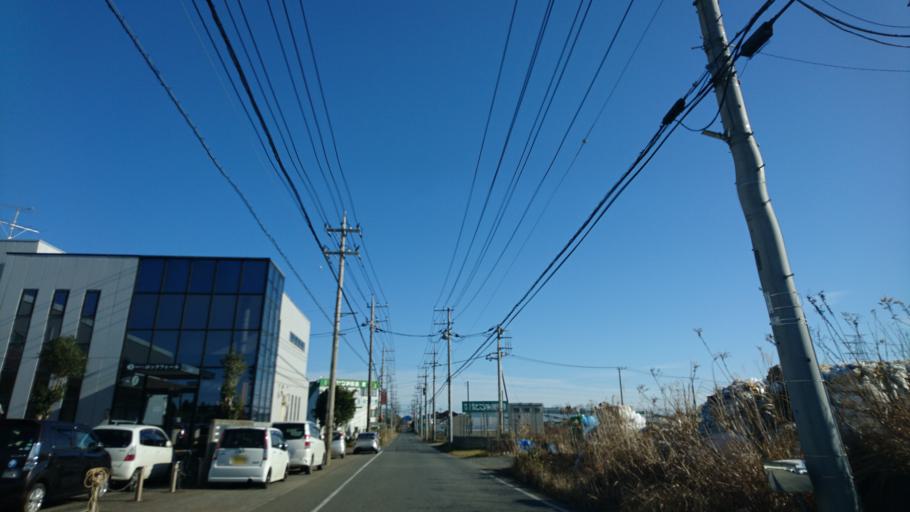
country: JP
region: Chiba
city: Togane
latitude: 35.5865
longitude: 140.3166
